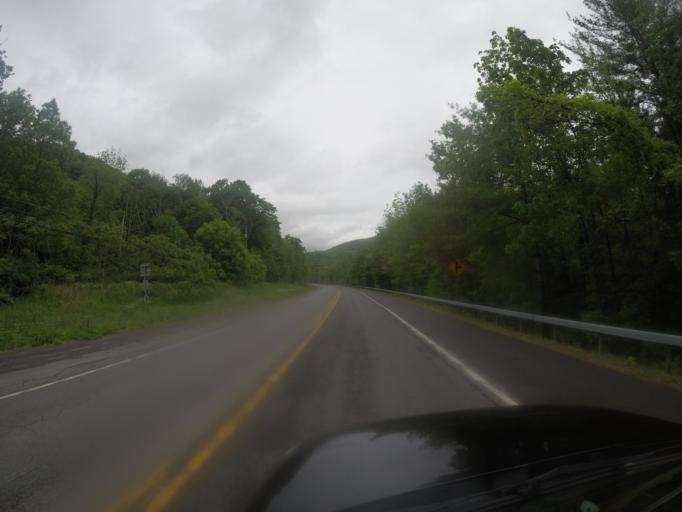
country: US
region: New York
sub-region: Ulster County
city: Shokan
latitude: 42.0745
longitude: -74.3070
